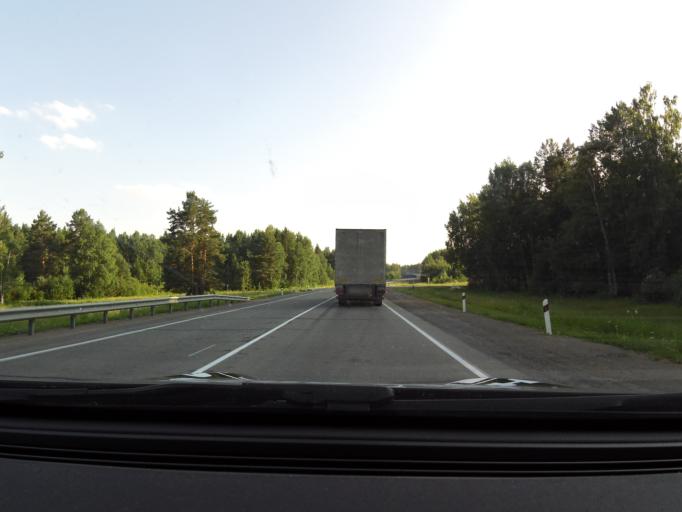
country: RU
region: Sverdlovsk
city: Druzhinino
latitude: 56.7878
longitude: 59.4605
